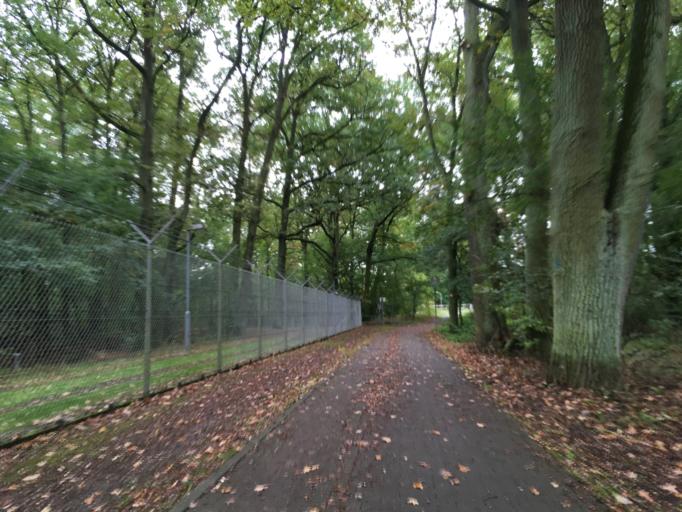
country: DE
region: Brandenburg
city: Ahrensfelde
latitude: 52.5933
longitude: 13.5827
